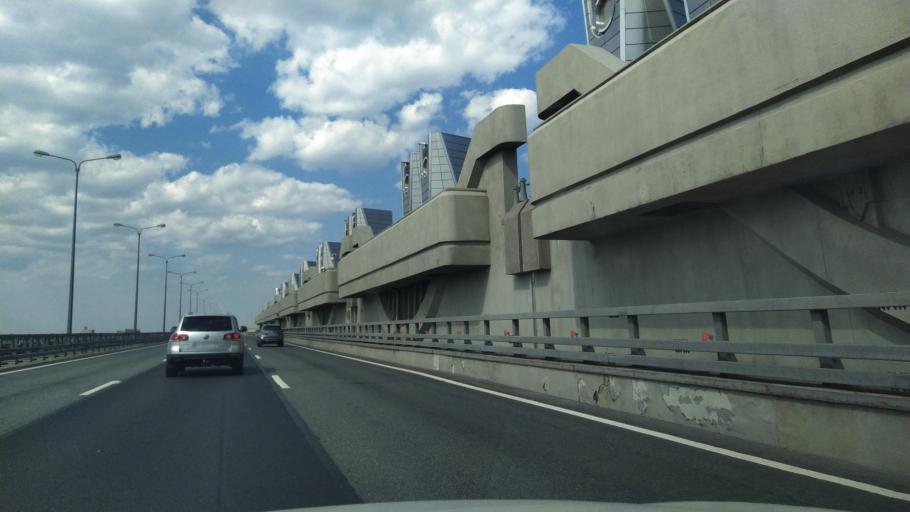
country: RU
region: Leningrad
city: Gorskaya
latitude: 60.0375
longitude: 29.9521
